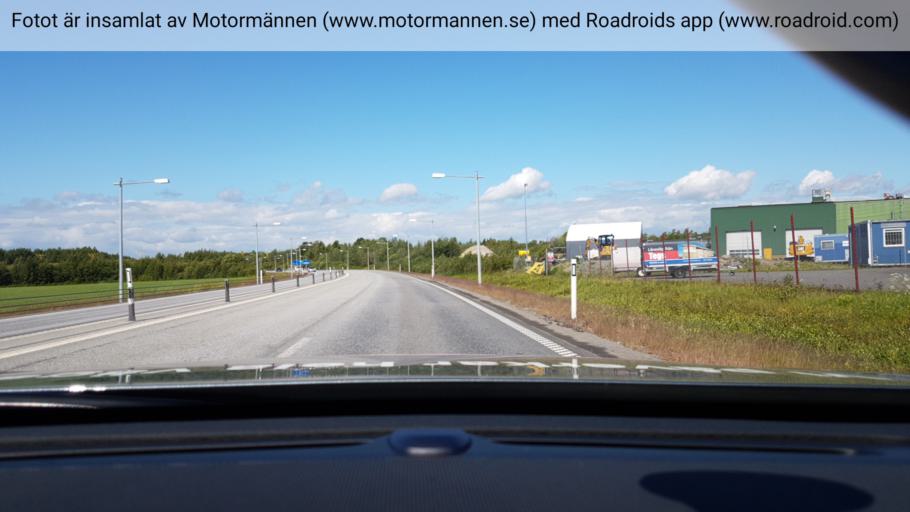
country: SE
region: Vaesterbotten
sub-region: Umea Kommun
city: Umea
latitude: 63.8017
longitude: 20.2689
